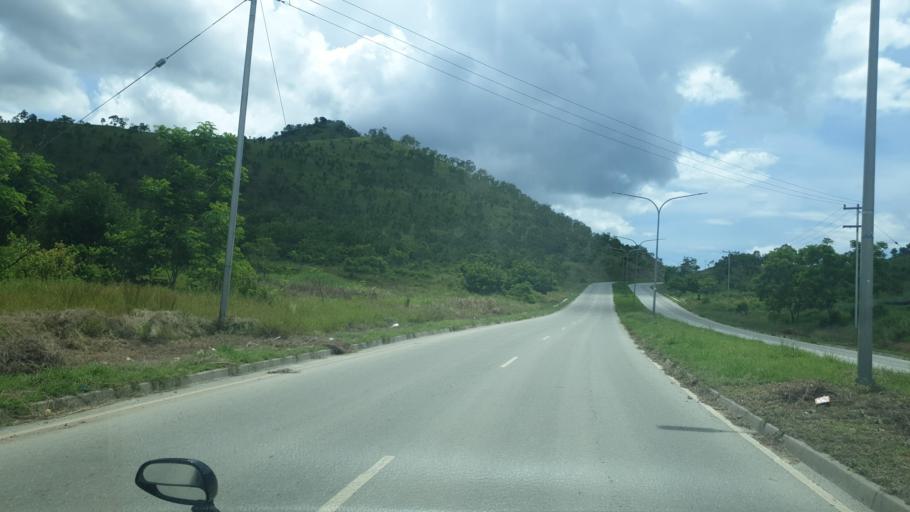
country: PG
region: National Capital
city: Port Moresby
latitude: -9.4208
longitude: 147.1374
